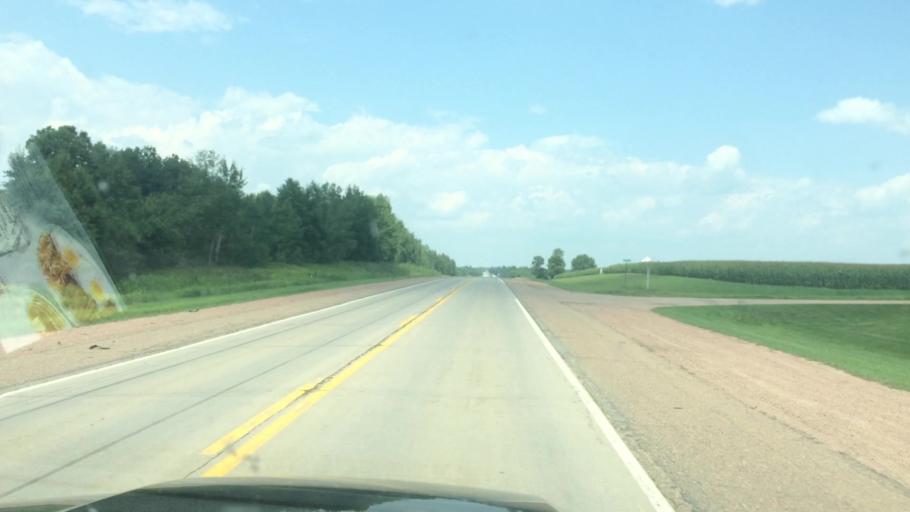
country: US
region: Wisconsin
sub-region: Clark County
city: Colby
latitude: 44.8802
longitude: -90.3156
